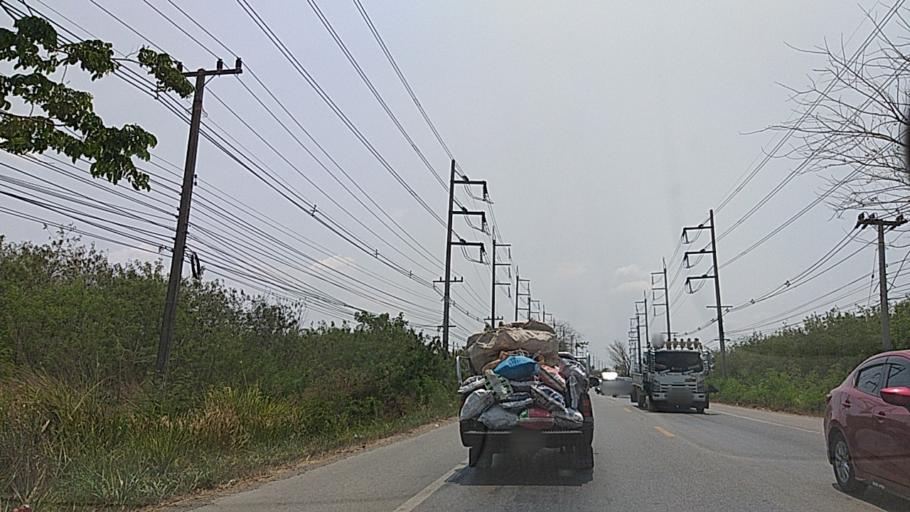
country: TH
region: Chachoengsao
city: Bang Nam Priao
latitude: 13.8050
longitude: 101.0535
